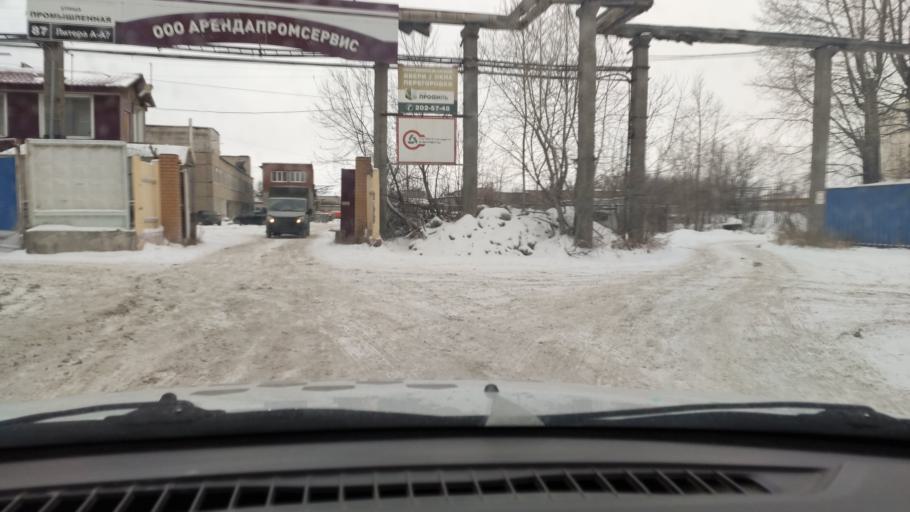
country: RU
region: Perm
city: Kondratovo
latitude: 57.9453
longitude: 56.1357
